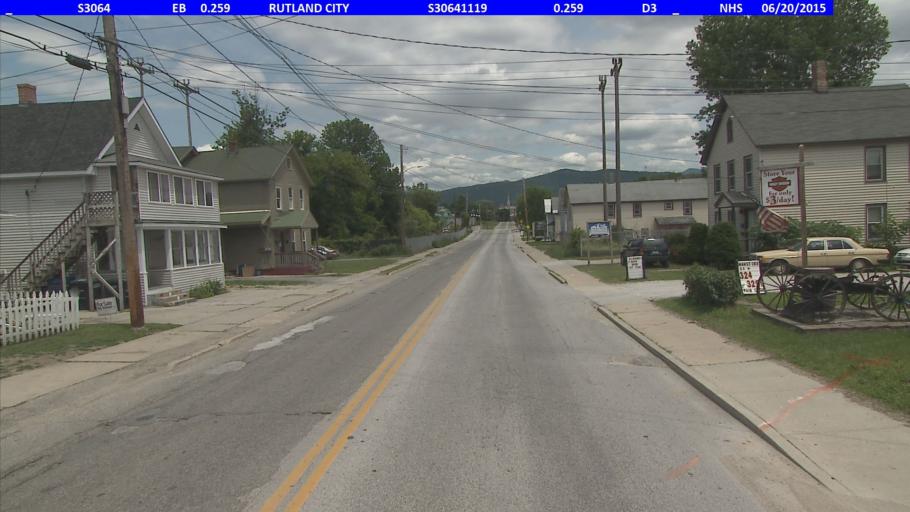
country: US
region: Vermont
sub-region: Rutland County
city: Rutland
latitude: 43.6062
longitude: -72.9901
